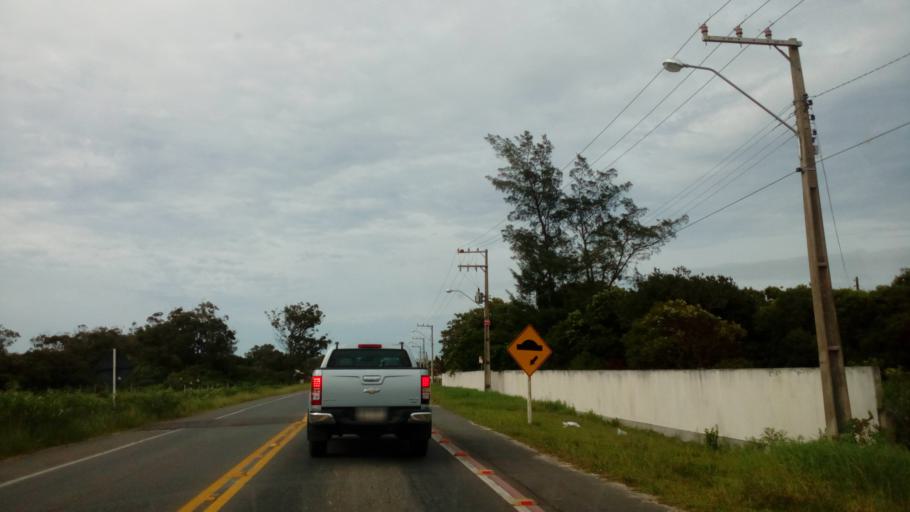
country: BR
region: Santa Catarina
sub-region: Laguna
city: Laguna
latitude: -28.5557
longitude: -48.8017
